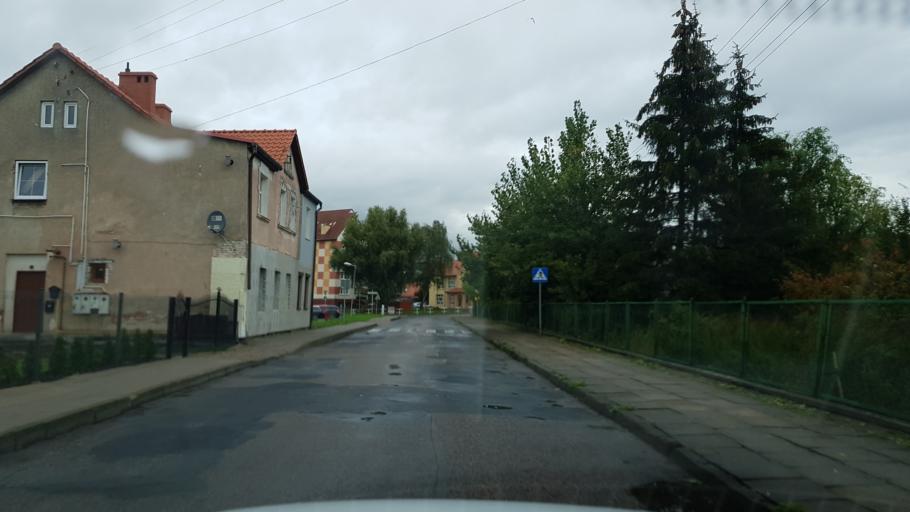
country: PL
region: West Pomeranian Voivodeship
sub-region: Powiat kamienski
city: Wolin
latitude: 53.8406
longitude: 14.6143
